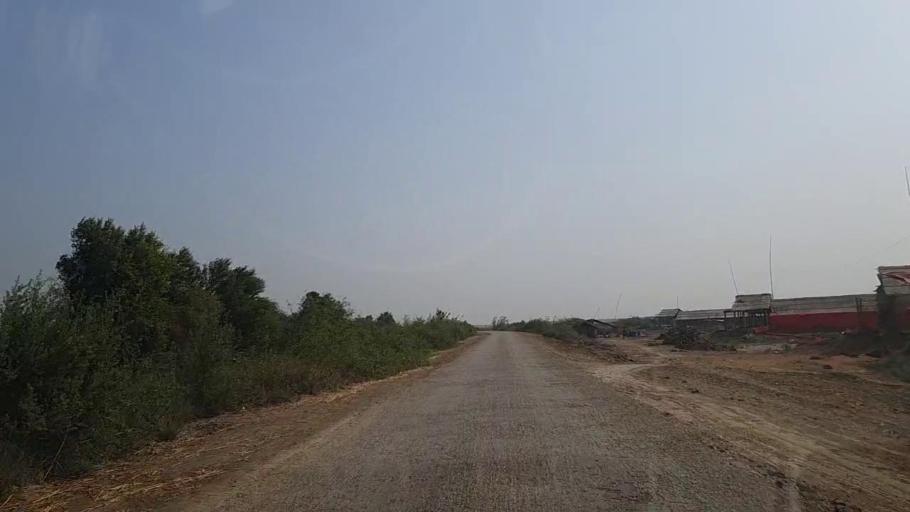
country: PK
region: Sindh
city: Keti Bandar
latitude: 24.2348
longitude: 67.6423
